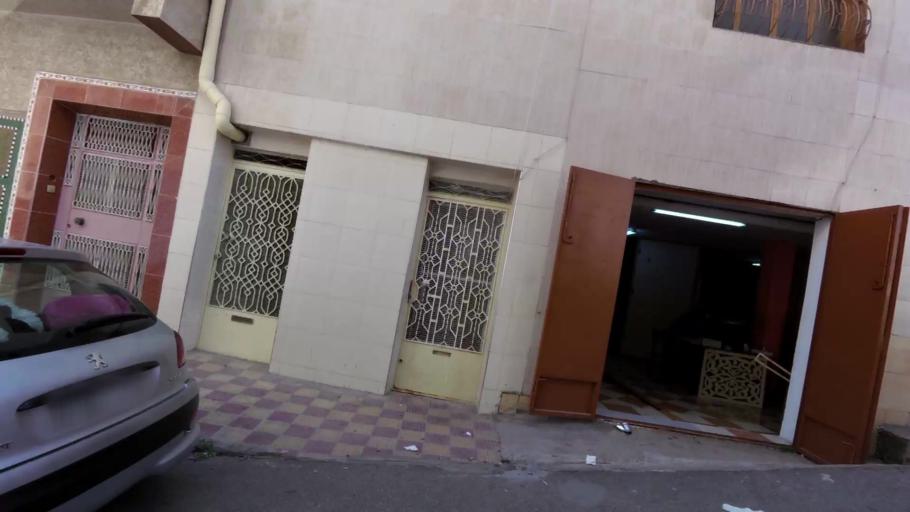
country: MA
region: Tanger-Tetouan
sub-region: Tanger-Assilah
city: Tangier
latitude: 35.7533
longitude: -5.8276
